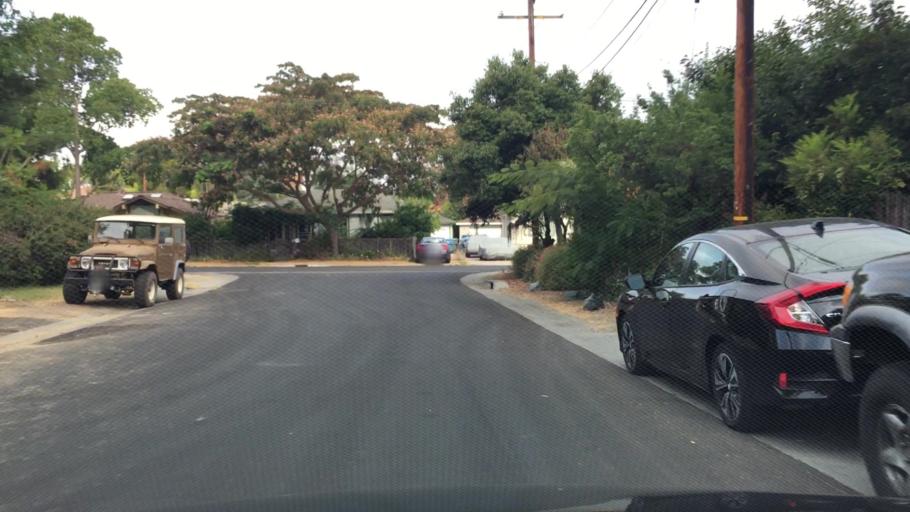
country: US
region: California
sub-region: Santa Clara County
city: Los Altos
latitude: 37.4101
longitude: -122.1275
